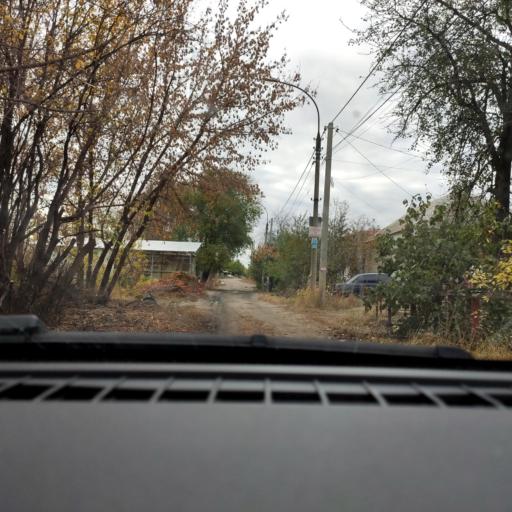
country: RU
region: Voronezj
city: Maslovka
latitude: 51.6193
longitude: 39.2609
